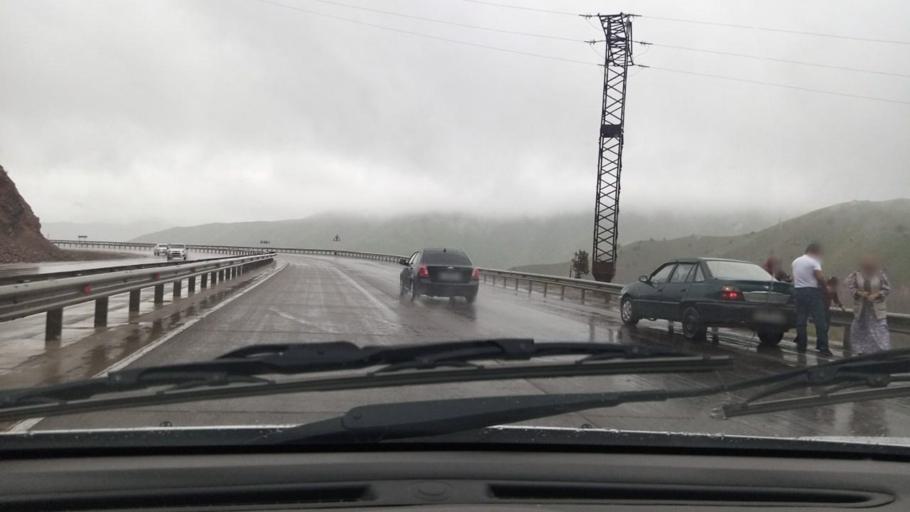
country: UZ
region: Toshkent
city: Angren
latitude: 41.0888
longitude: 70.5353
